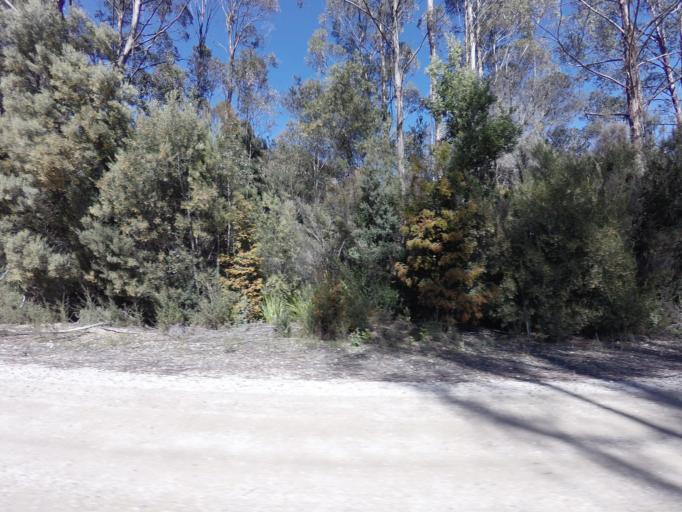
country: AU
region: Tasmania
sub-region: Huon Valley
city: Geeveston
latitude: -42.8706
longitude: 146.3736
